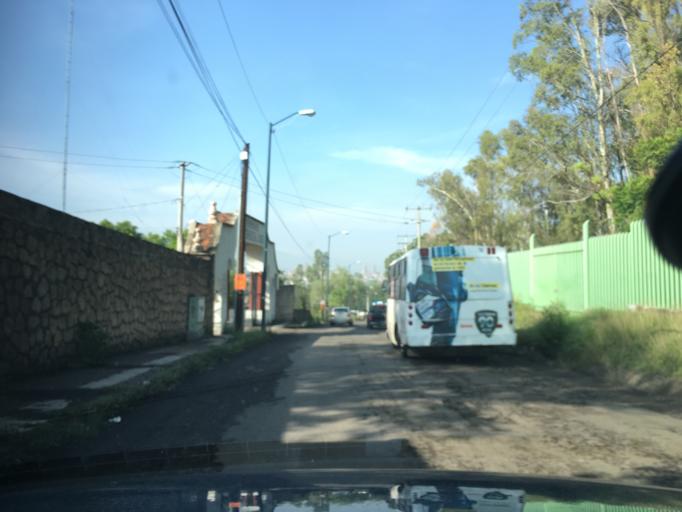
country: MX
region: Michoacan
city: Morelia
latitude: 19.7217
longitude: -101.1830
